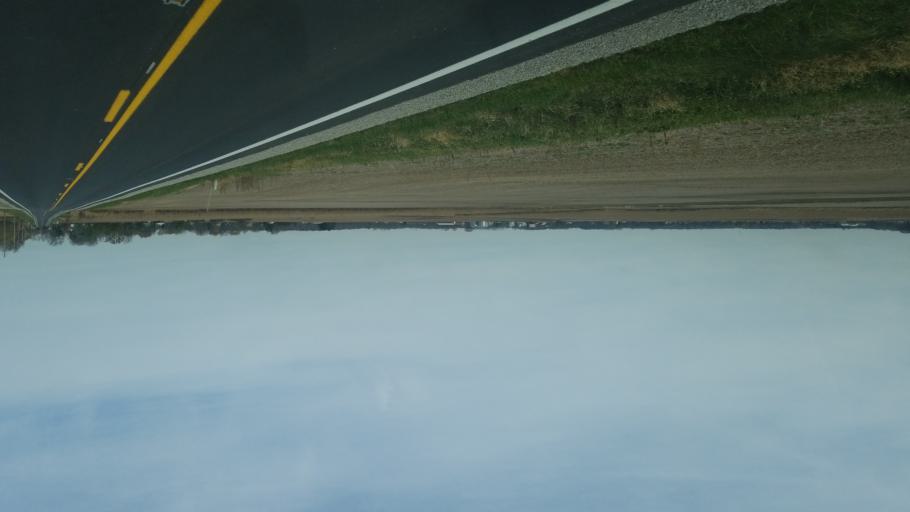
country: US
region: Ohio
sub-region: Madison County
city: Choctaw Lake
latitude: 39.9259
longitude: -83.4873
